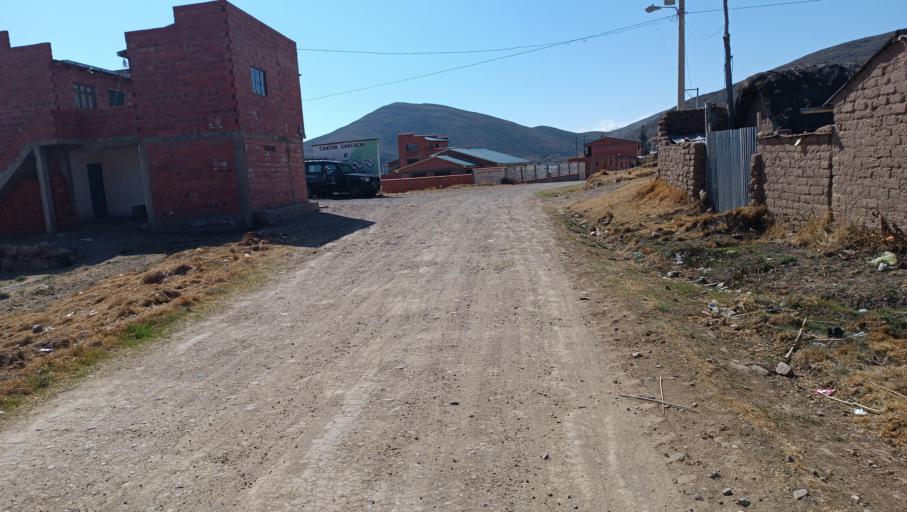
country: BO
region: La Paz
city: Huatajata
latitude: -16.3452
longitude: -68.6753
